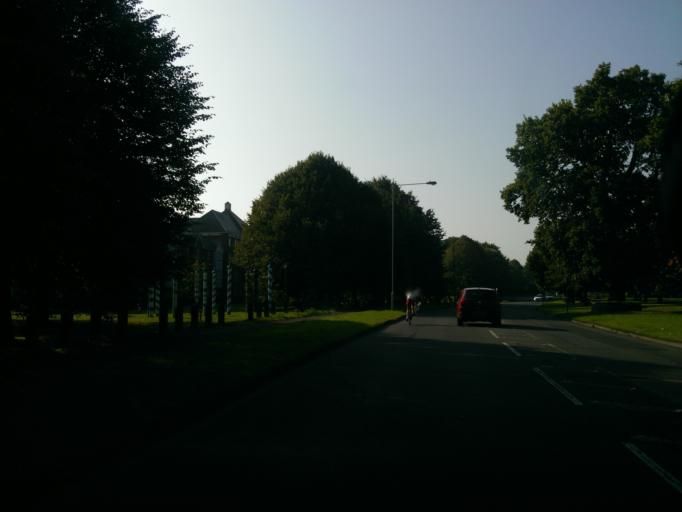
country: GB
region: England
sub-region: Essex
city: Layer de la Haye
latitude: 51.8689
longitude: 0.8755
